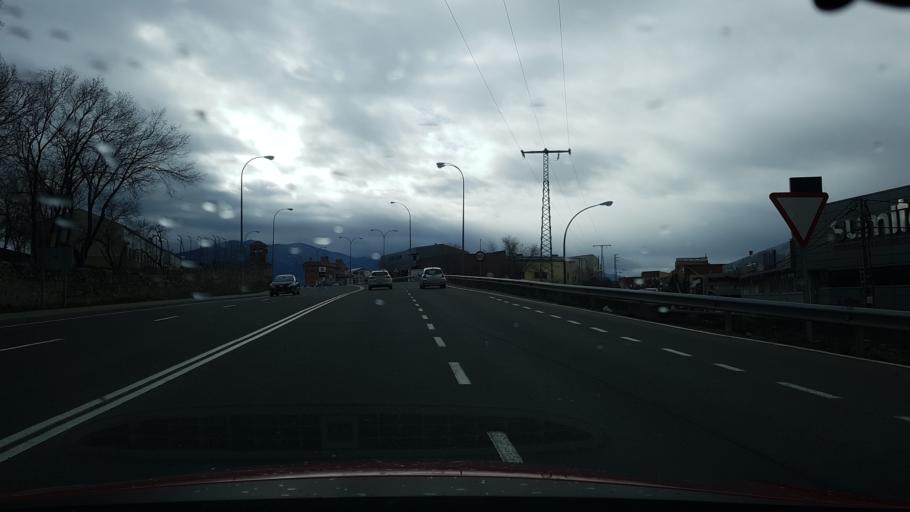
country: ES
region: Castille and Leon
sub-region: Provincia de Segovia
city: Segovia
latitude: 40.9305
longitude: -4.1101
